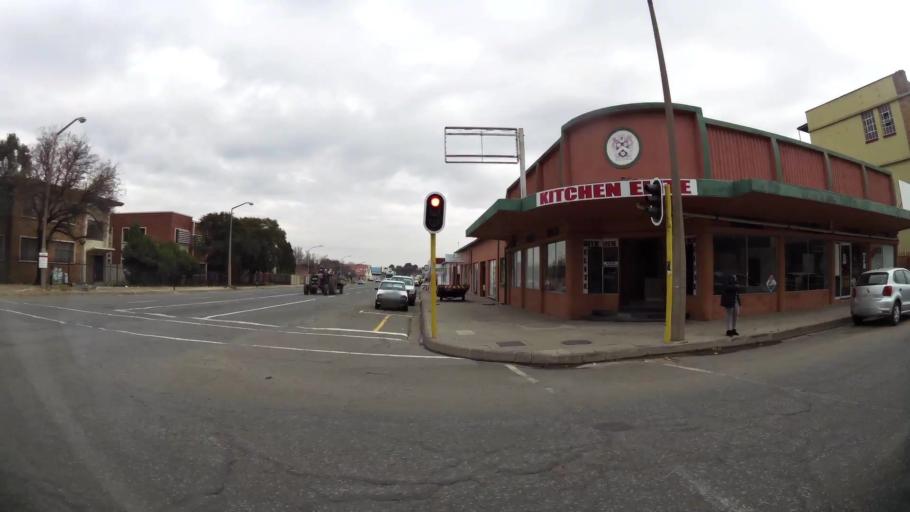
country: ZA
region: Orange Free State
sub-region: Fezile Dabi District Municipality
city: Kroonstad
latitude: -27.6637
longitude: 27.2324
